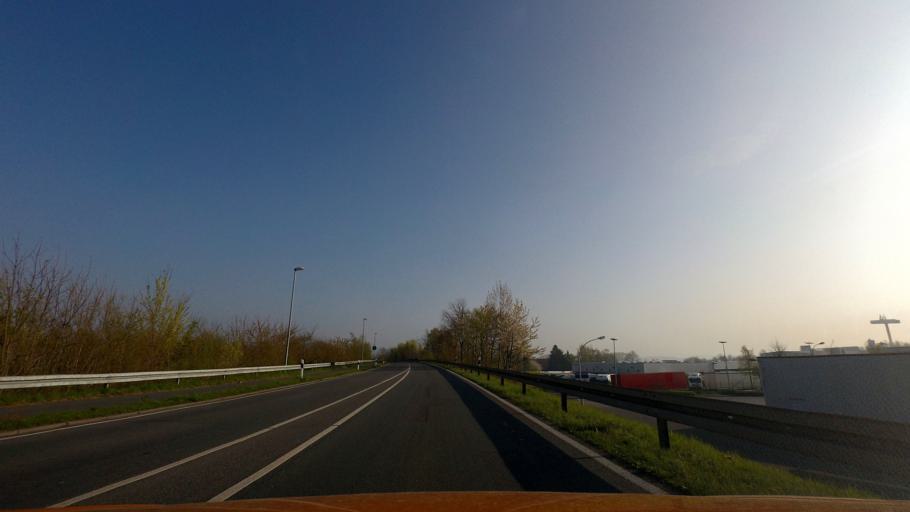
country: DE
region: Lower Saxony
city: Melle
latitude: 52.1932
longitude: 8.3554
